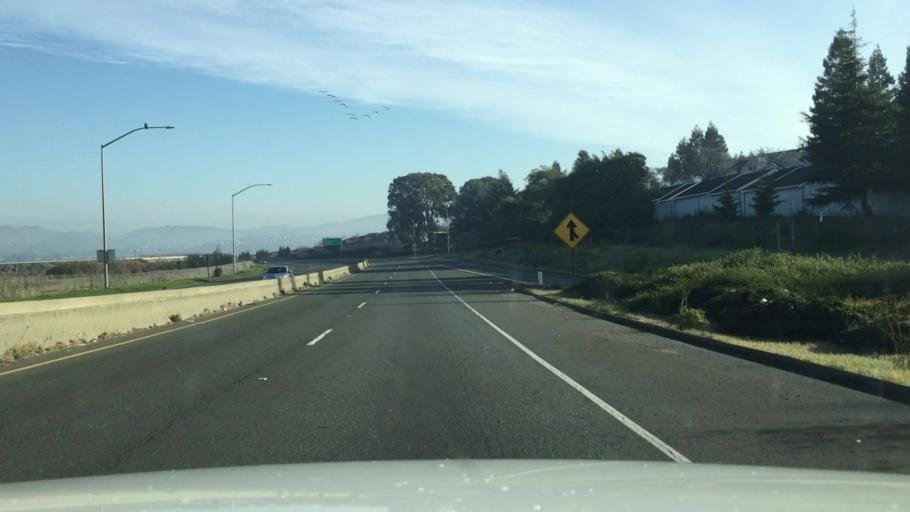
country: US
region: California
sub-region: Solano County
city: Vallejo
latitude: 38.1224
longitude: -122.2748
